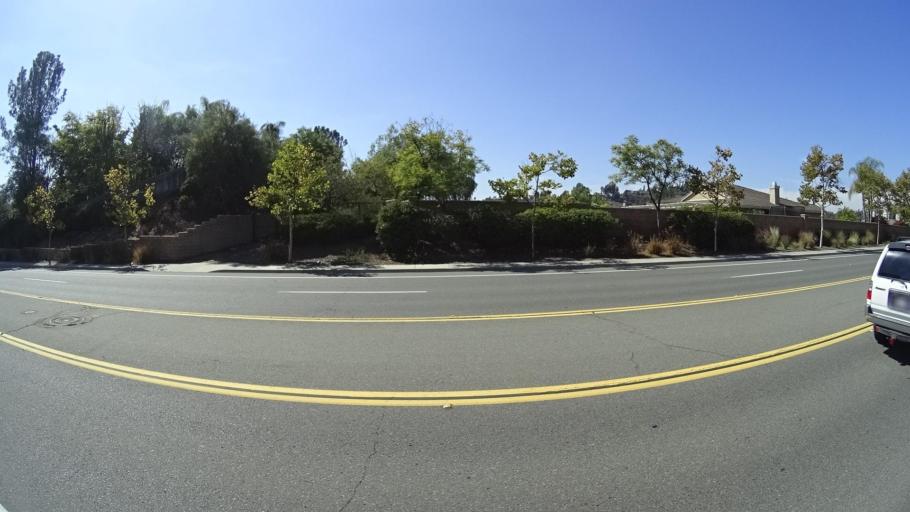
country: US
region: California
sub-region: San Diego County
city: Rancho San Diego
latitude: 32.7659
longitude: -116.9235
